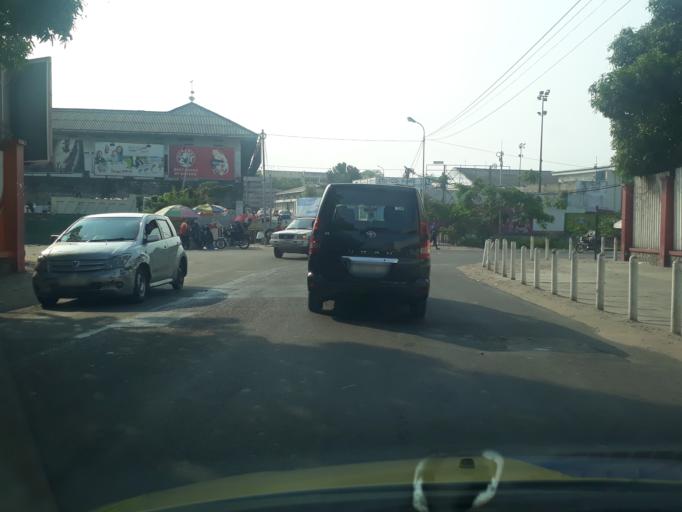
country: CD
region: Kinshasa
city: Kinshasa
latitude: -4.3076
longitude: 15.3259
